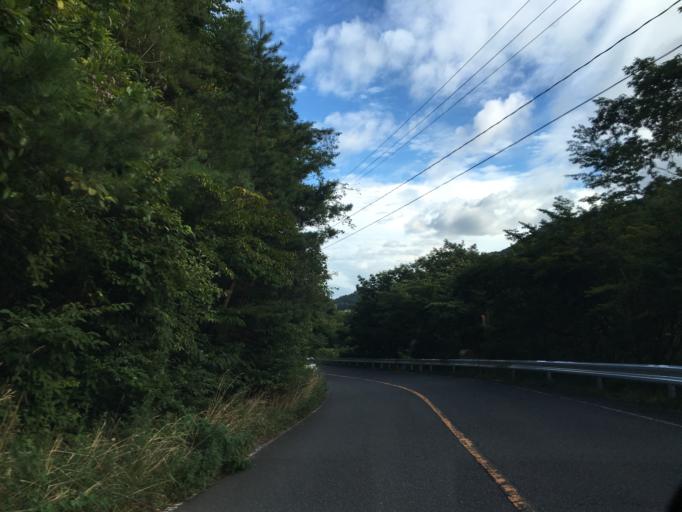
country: JP
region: Fukushima
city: Motomiya
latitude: 37.5089
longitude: 140.2737
